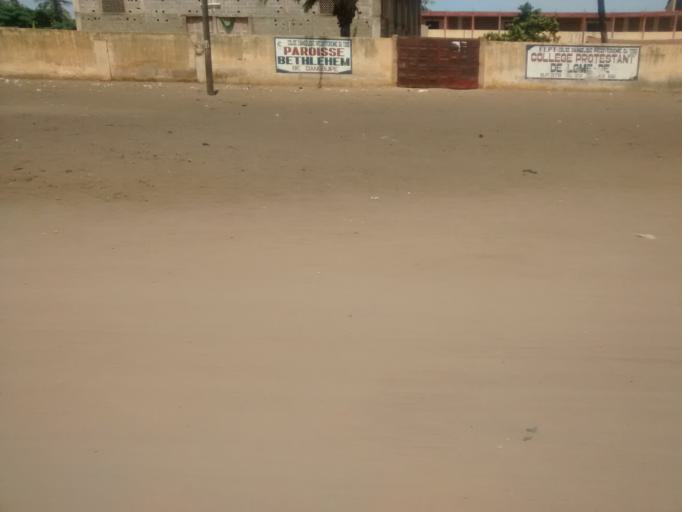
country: TG
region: Maritime
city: Lome
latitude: 6.1474
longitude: 1.2403
